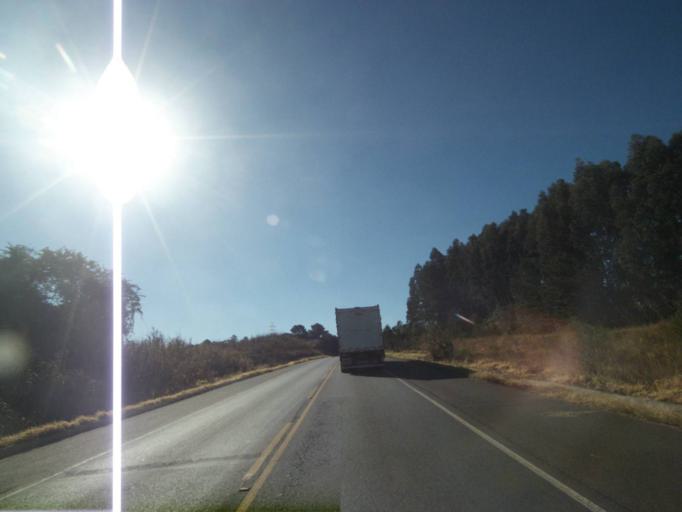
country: BR
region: Parana
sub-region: Tibagi
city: Tibagi
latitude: -24.5311
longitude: -50.4477
